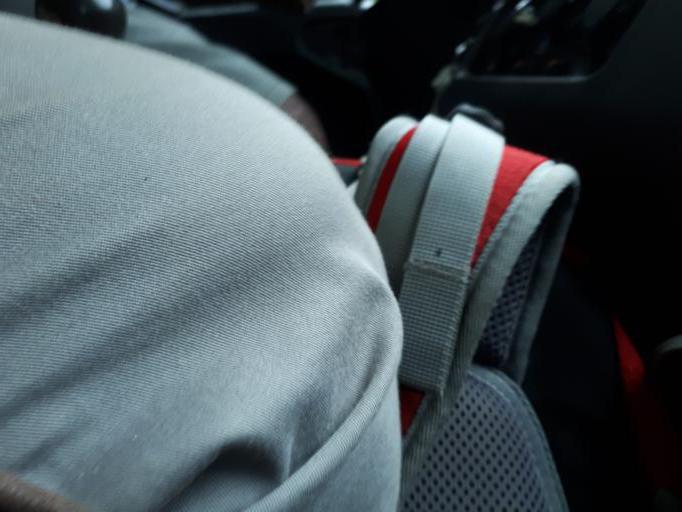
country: VU
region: Sanma
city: Luganville
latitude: -15.5727
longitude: 166.9402
